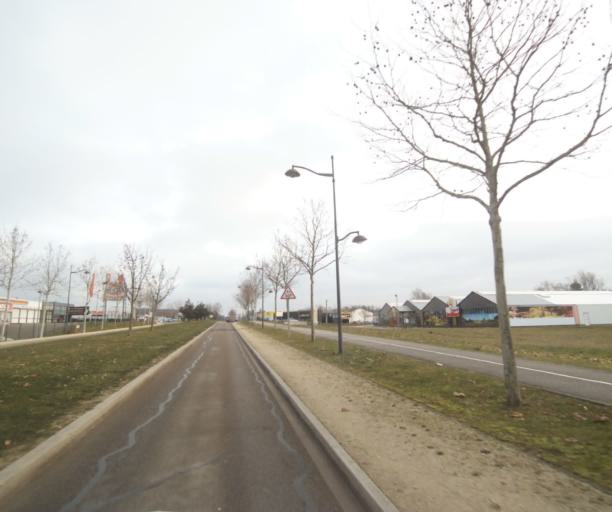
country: FR
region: Champagne-Ardenne
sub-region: Departement de la Haute-Marne
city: Bettancourt-la-Ferree
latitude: 48.6511
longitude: 4.9618
